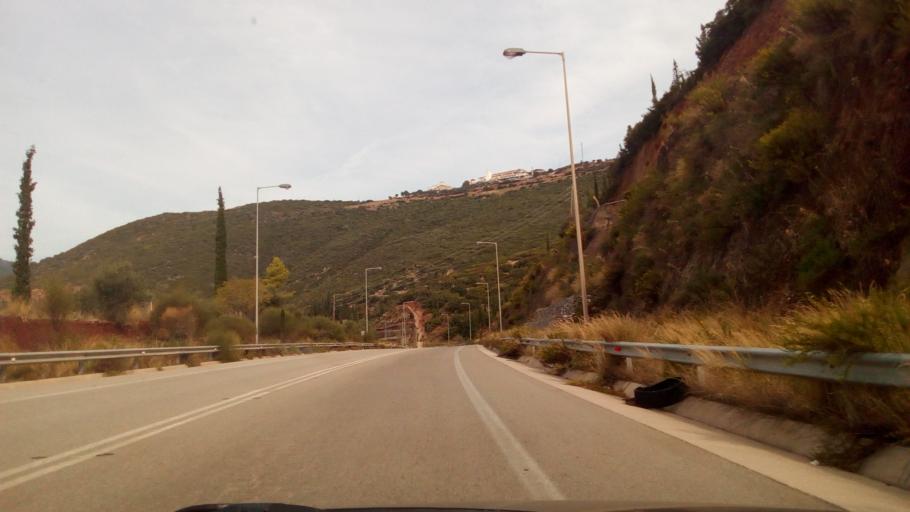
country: GR
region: West Greece
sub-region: Nomos Aitolias kai Akarnanias
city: Nafpaktos
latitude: 38.4077
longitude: 21.8555
